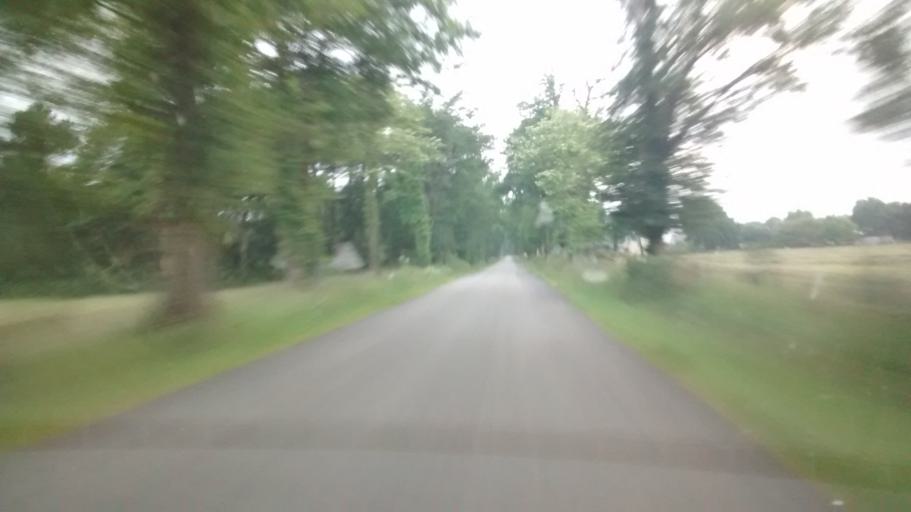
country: FR
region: Brittany
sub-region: Departement du Morbihan
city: Pleucadeuc
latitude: 47.7357
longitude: -2.3423
